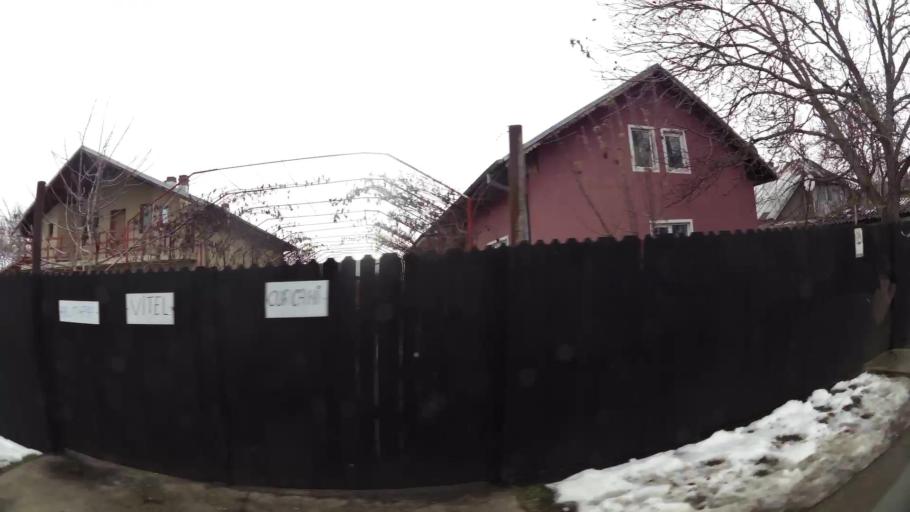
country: RO
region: Ilfov
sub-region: Comuna Tunari
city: Tunari
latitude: 44.5475
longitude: 26.1289
